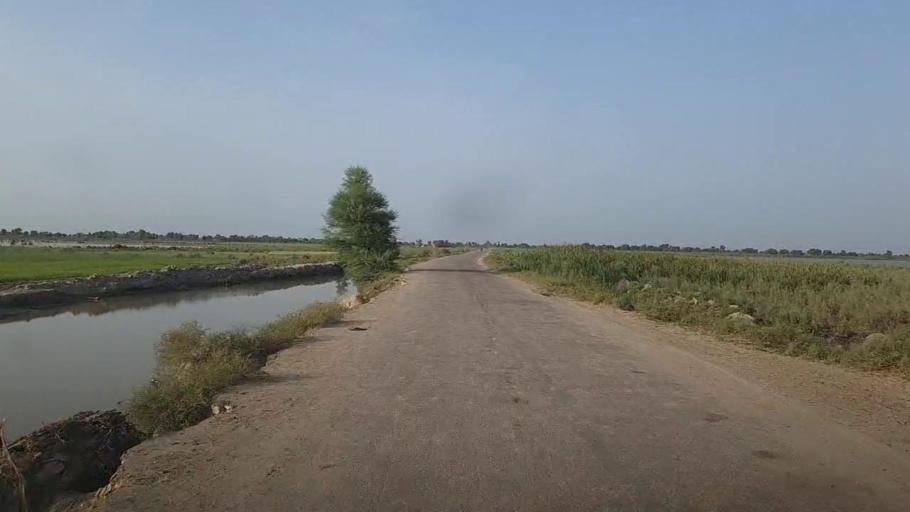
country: PK
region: Sindh
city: Khairpur
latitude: 28.0896
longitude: 69.8032
